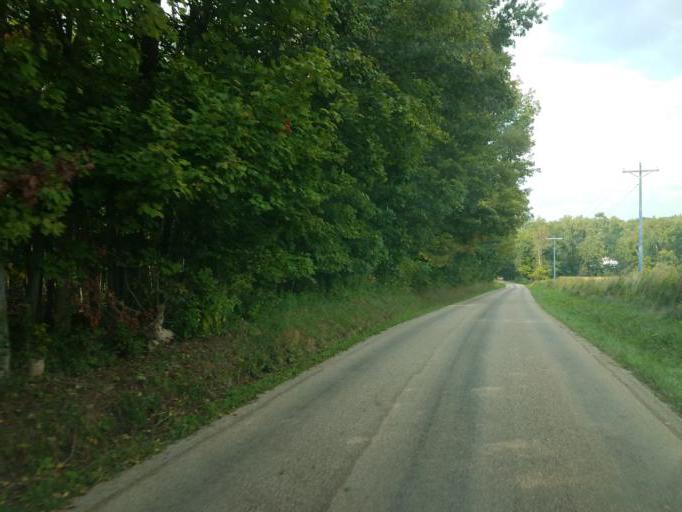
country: US
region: Ohio
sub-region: Knox County
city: Gambier
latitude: 40.3422
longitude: -82.3876
